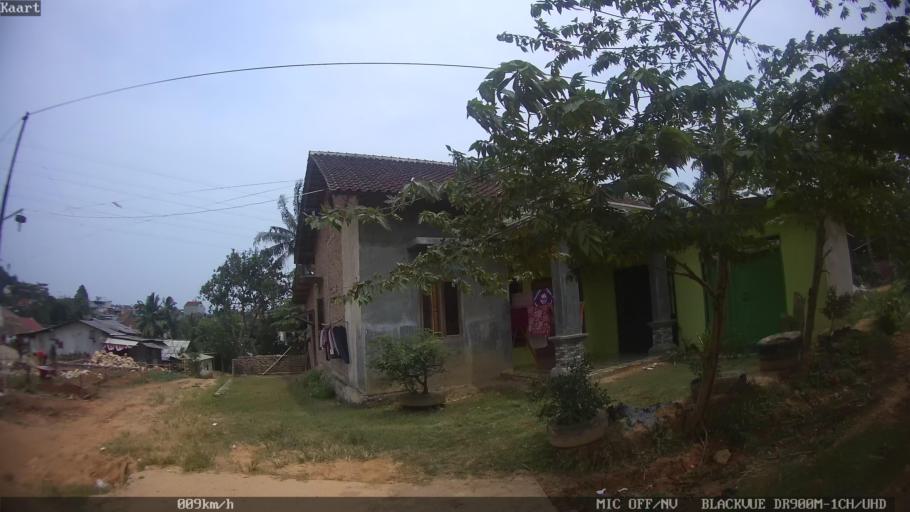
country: ID
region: Lampung
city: Kedaton
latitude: -5.4007
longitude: 105.3265
